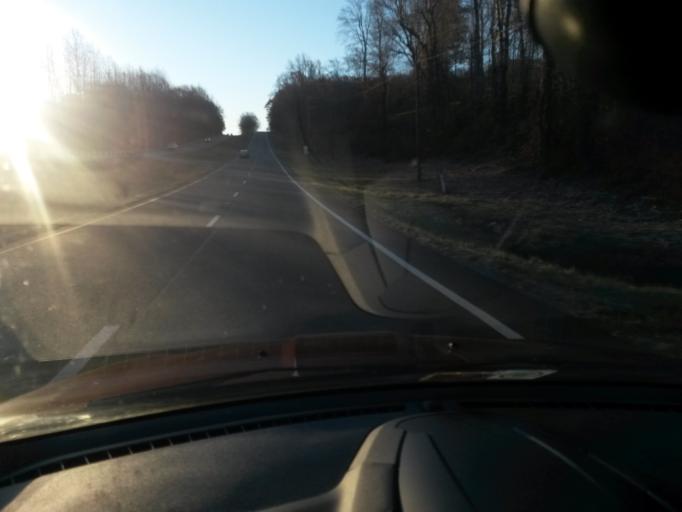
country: US
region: Virginia
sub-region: Franklin County
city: Henry Fork
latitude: 36.9465
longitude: -79.8800
